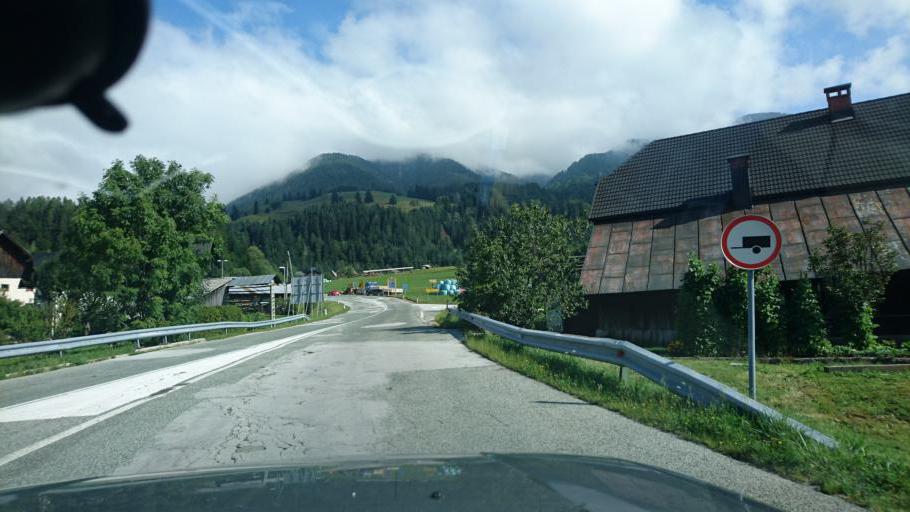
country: SI
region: Kranjska Gora
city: Kranjska Gora
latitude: 46.4919
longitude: 13.7581
